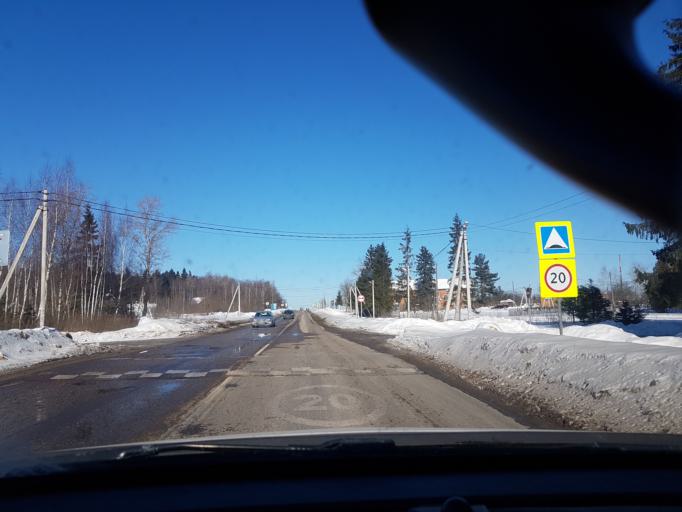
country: RU
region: Moskovskaya
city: Sychevo
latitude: 56.0115
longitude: 36.2184
